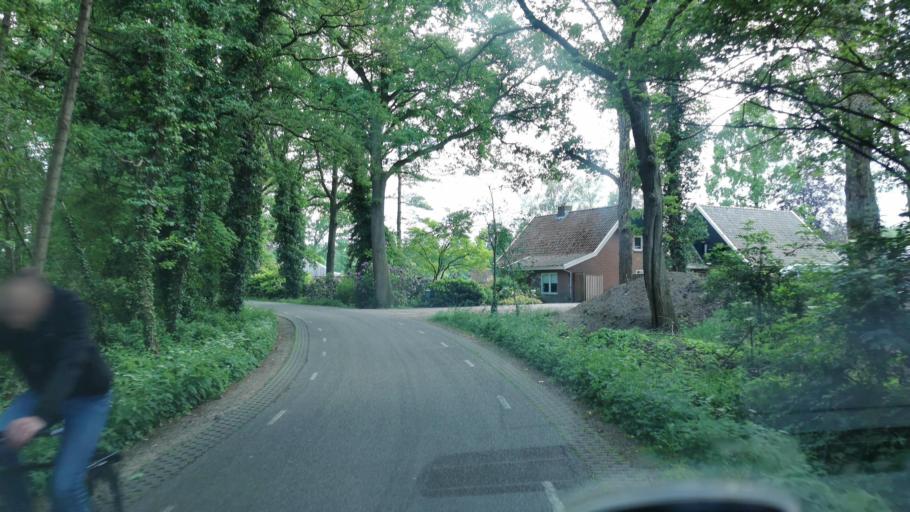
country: NL
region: Overijssel
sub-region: Gemeente Hengelo
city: Hengelo
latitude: 52.3311
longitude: 6.8175
